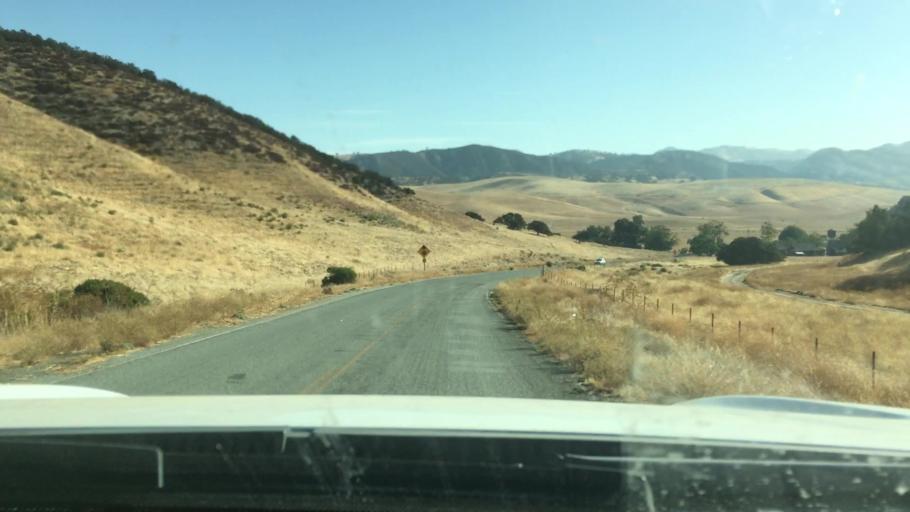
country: US
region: California
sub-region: Monterey County
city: King City
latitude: 36.3800
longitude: -121.0070
